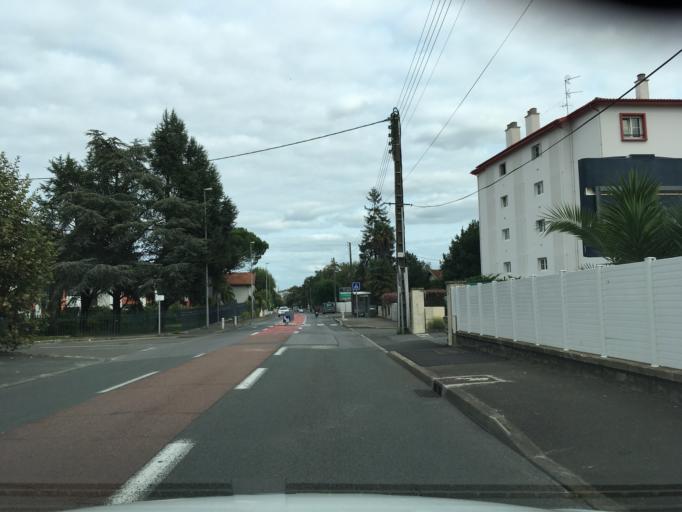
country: FR
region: Aquitaine
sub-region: Departement des Pyrenees-Atlantiques
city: Anglet
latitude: 43.4803
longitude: -1.5268
